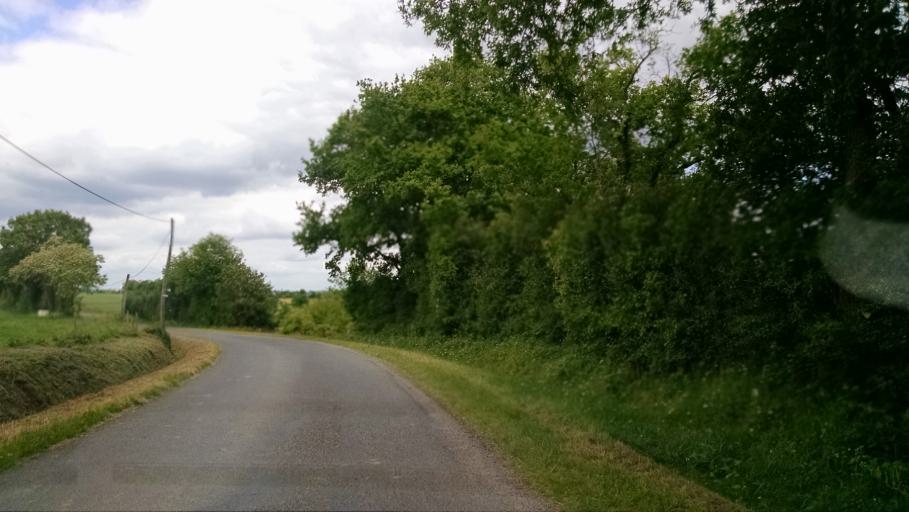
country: FR
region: Pays de la Loire
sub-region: Departement de la Loire-Atlantique
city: Remouille
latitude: 47.0367
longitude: -1.3833
